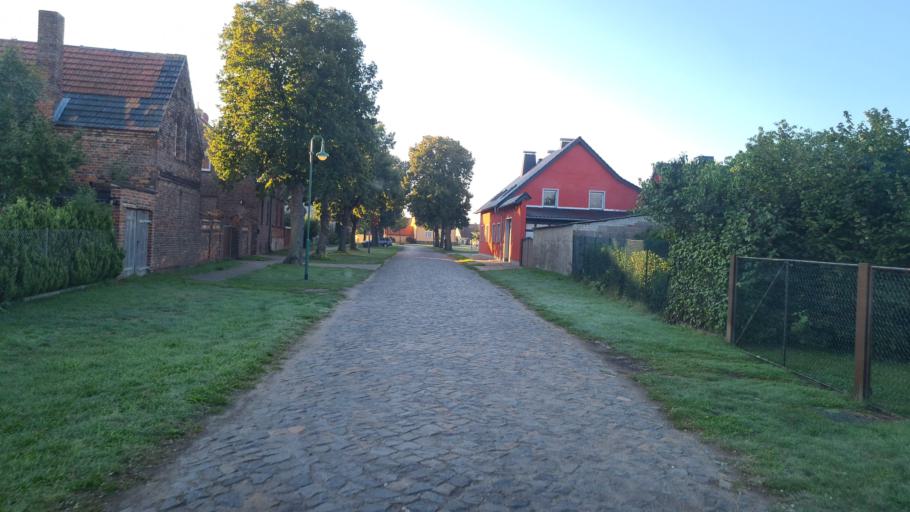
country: DE
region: Saxony-Anhalt
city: Holzdorf
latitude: 51.8077
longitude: 13.1159
